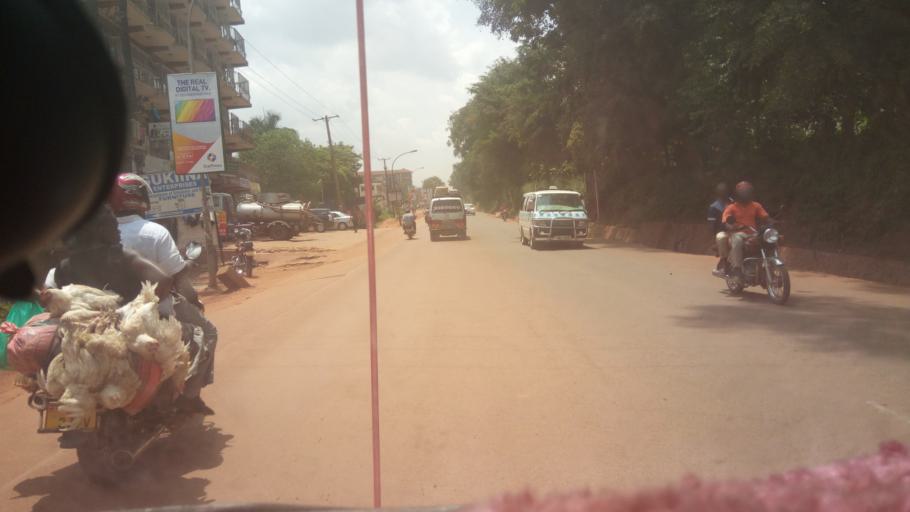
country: UG
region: Central Region
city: Kampala Central Division
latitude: 0.3294
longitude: 32.5649
